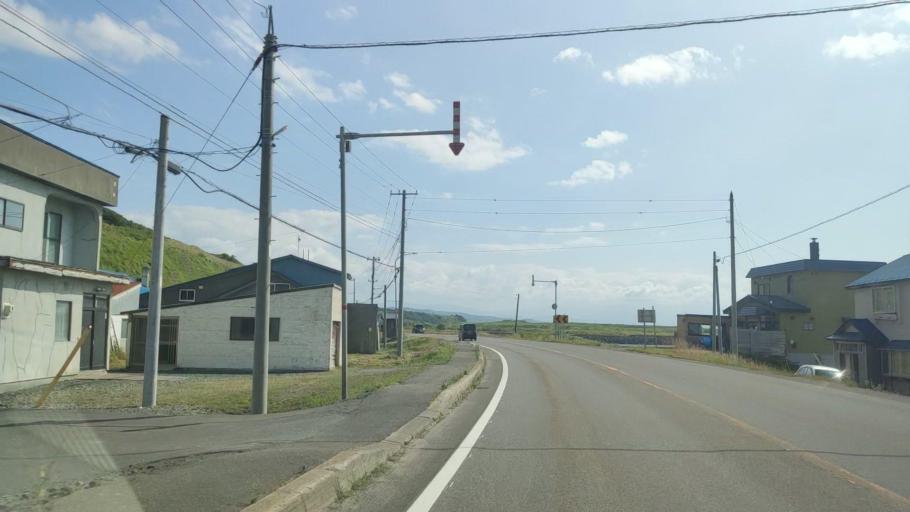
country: JP
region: Hokkaido
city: Rumoi
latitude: 43.9794
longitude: 141.6465
